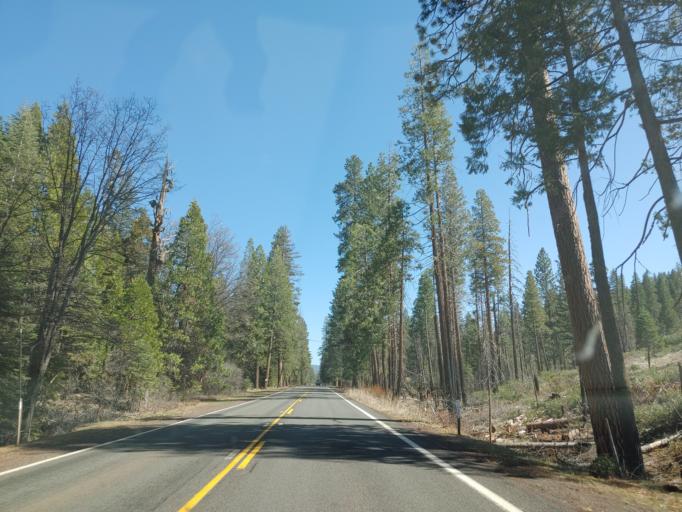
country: US
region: California
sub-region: Shasta County
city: Burney
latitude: 40.7567
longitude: -121.4952
